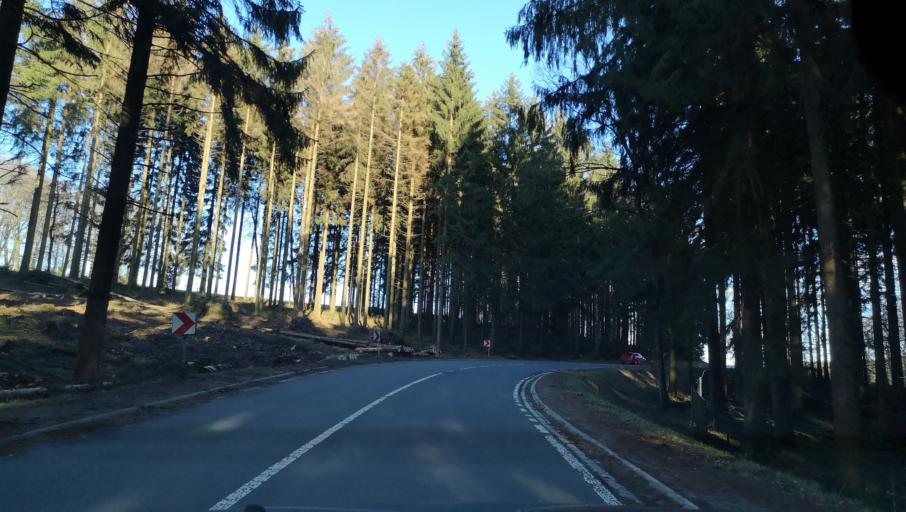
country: DE
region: North Rhine-Westphalia
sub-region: Regierungsbezirk Arnsberg
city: Breckerfeld
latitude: 51.2406
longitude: 7.4140
